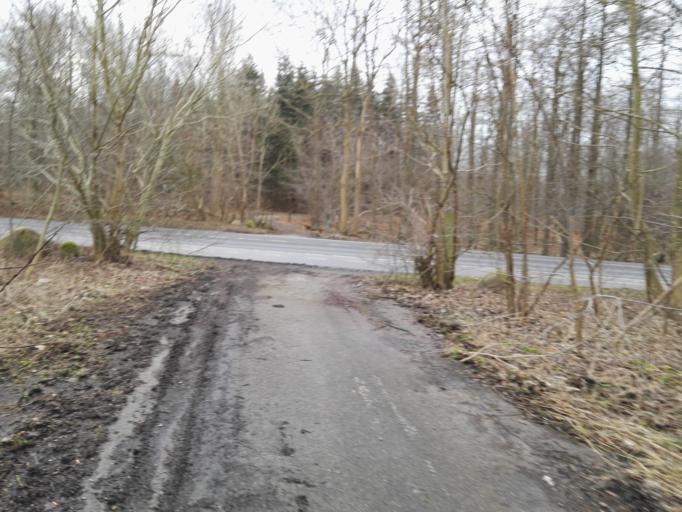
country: DK
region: Zealand
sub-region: Lejre Kommune
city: Lejre
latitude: 55.6476
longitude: 11.9234
